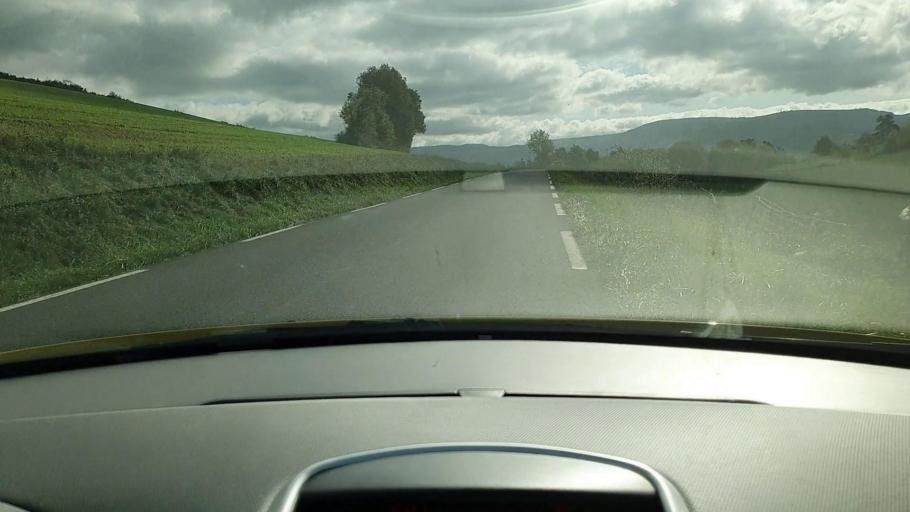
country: FR
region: Languedoc-Roussillon
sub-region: Departement de la Lozere
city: Meyrueis
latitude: 44.1285
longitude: 3.4054
